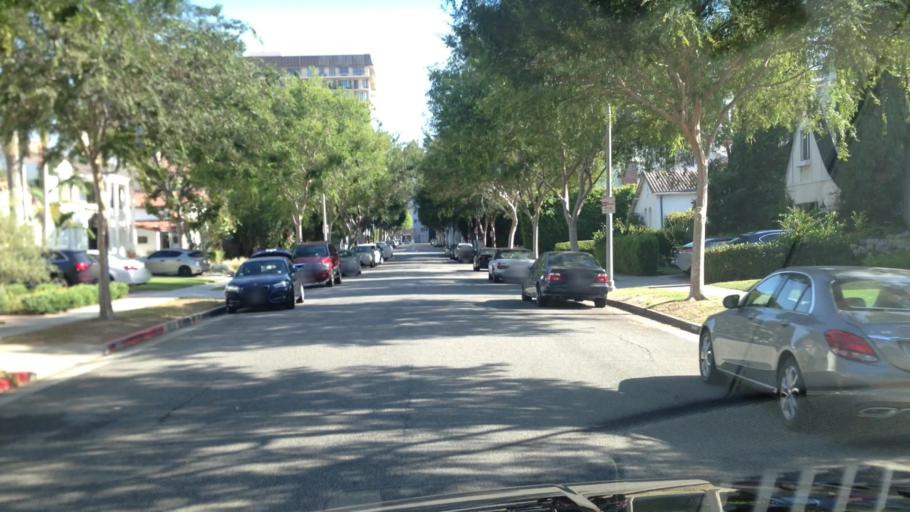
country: US
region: California
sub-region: Los Angeles County
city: Beverly Hills
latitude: 34.0637
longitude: -118.4002
